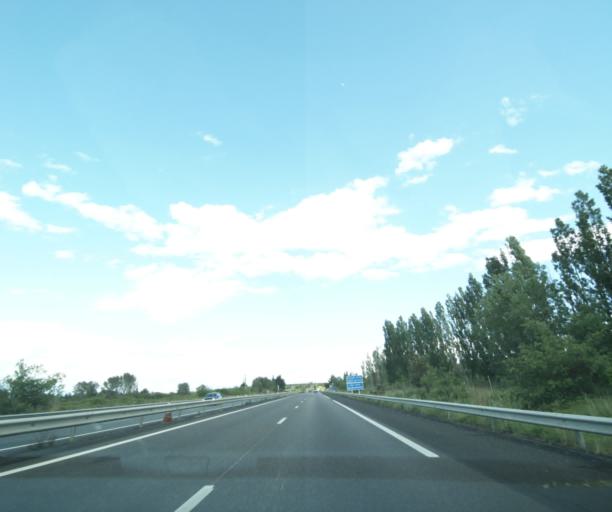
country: FR
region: Languedoc-Roussillon
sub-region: Departement du Gard
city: Garons
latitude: 43.7417
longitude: 4.4495
